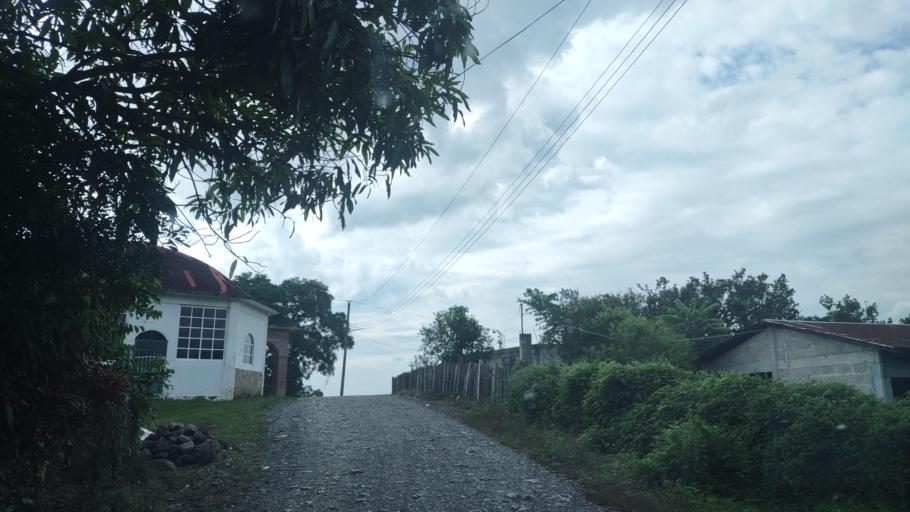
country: MX
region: Veracruz
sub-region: Ixcatepec
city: Ixcatepec
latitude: 21.2152
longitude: -97.9840
